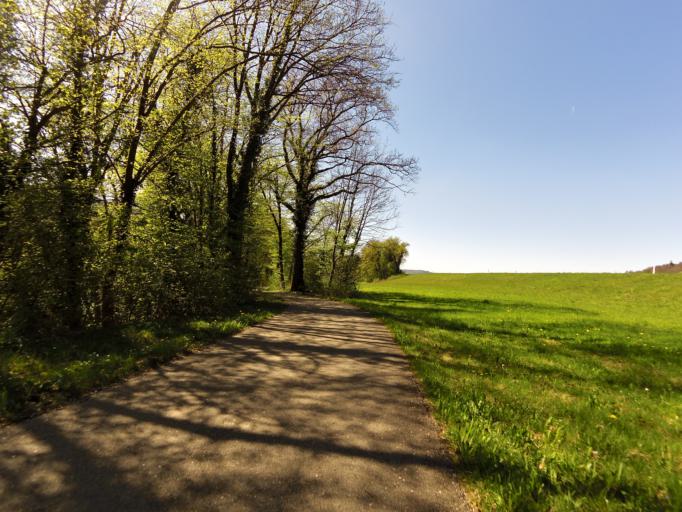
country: CH
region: Aargau
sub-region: Bezirk Zurzach
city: Bad Zurzach
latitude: 47.5716
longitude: 8.3476
